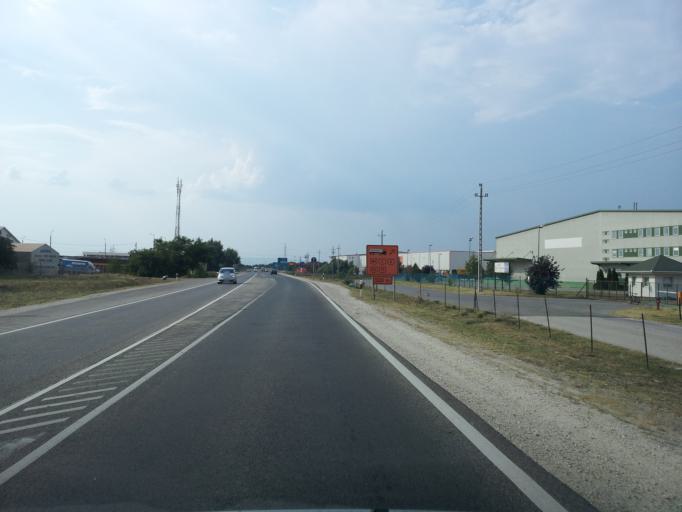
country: HU
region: Pest
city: Dunaharaszti
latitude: 47.3615
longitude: 19.1207
